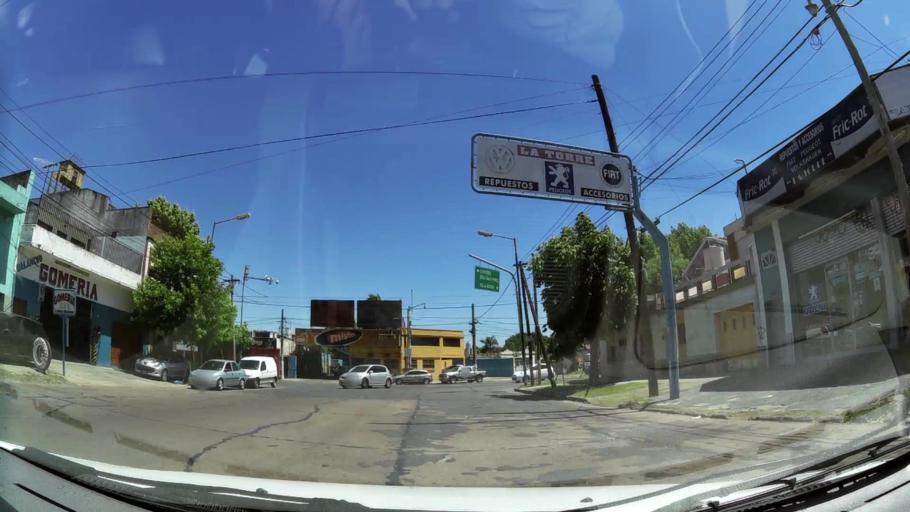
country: AR
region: Buenos Aires
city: Caseros
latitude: -34.5895
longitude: -58.5639
